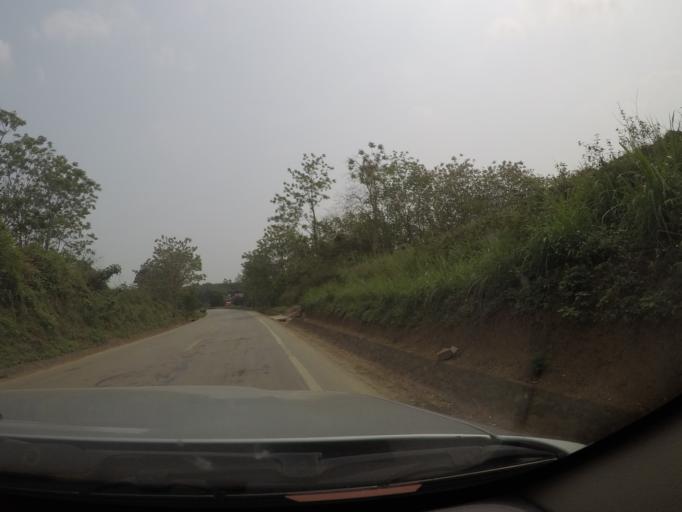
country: VN
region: Thanh Hoa
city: Thi Tran Yen Cat
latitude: 19.4845
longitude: 105.3942
